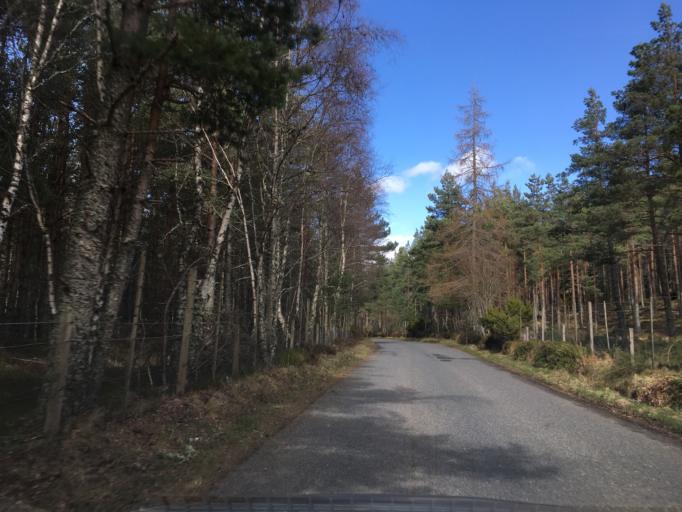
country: GB
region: Scotland
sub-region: Highland
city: Aviemore
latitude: 57.1960
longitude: -3.7990
